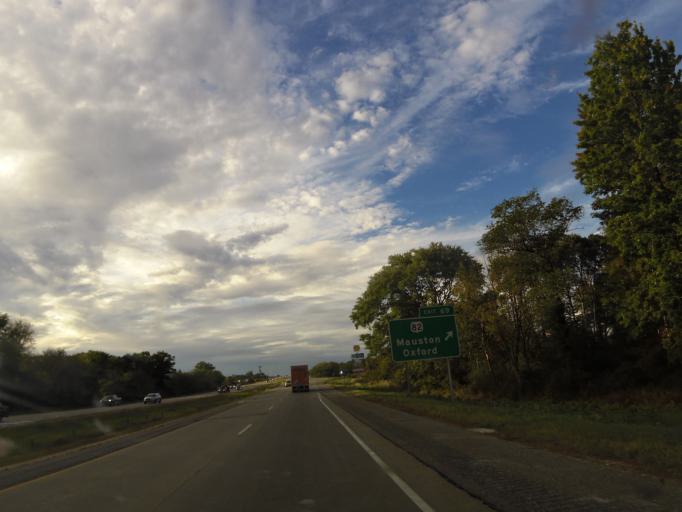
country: US
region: Wisconsin
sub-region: Juneau County
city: Mauston
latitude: 43.7924
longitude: -90.0526
